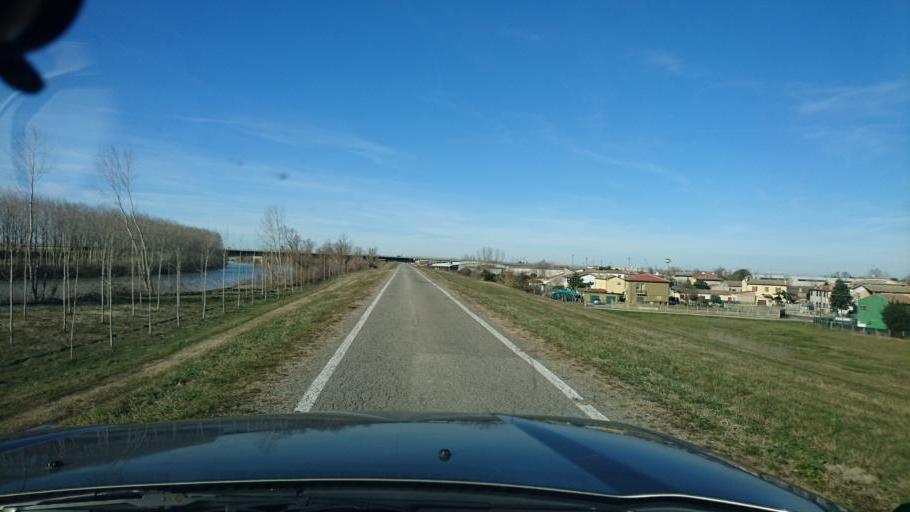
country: IT
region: Veneto
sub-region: Provincia di Rovigo
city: Ariano
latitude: 44.9375
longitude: 12.1293
